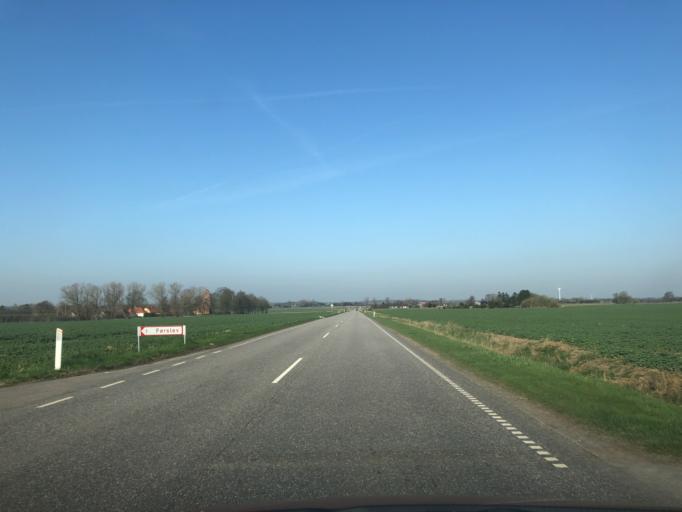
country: DK
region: Zealand
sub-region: Faxe Kommune
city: Haslev
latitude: 55.3580
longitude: 11.9131
